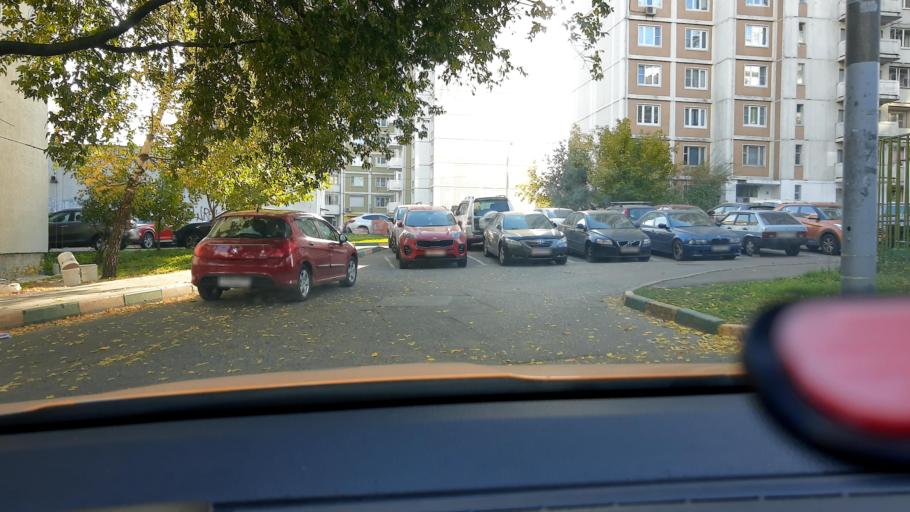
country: RU
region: Moskovskaya
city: Marfino
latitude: 55.7110
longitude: 37.3929
